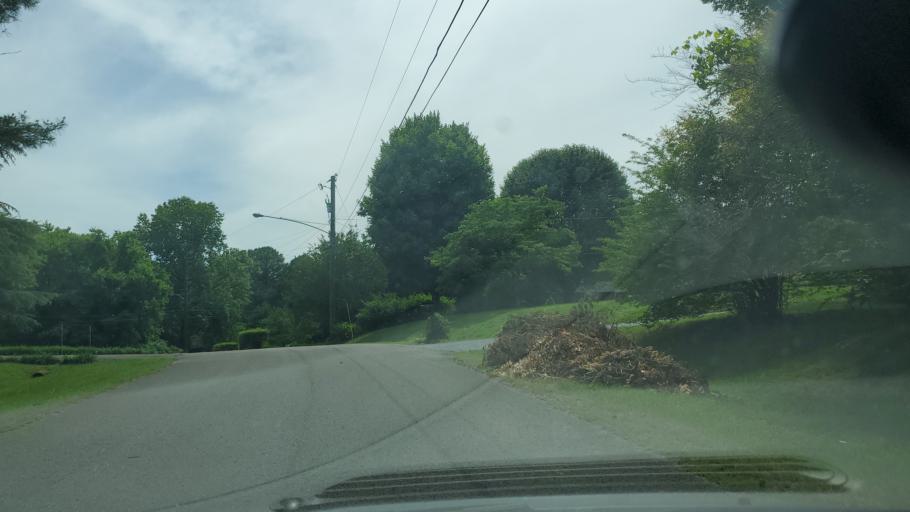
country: US
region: Tennessee
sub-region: Davidson County
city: Oak Hill
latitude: 36.1117
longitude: -86.6977
